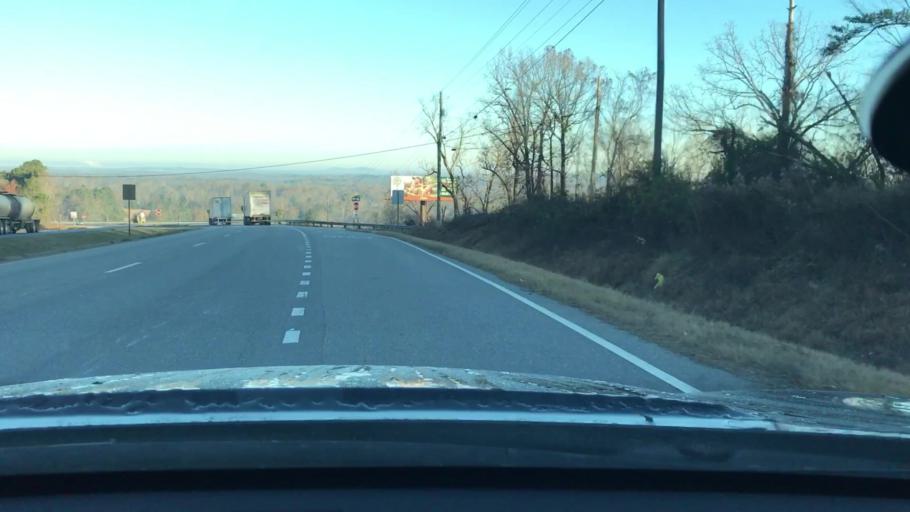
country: US
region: Alabama
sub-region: Talladega County
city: Mignon
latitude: 33.2026
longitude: -86.3074
